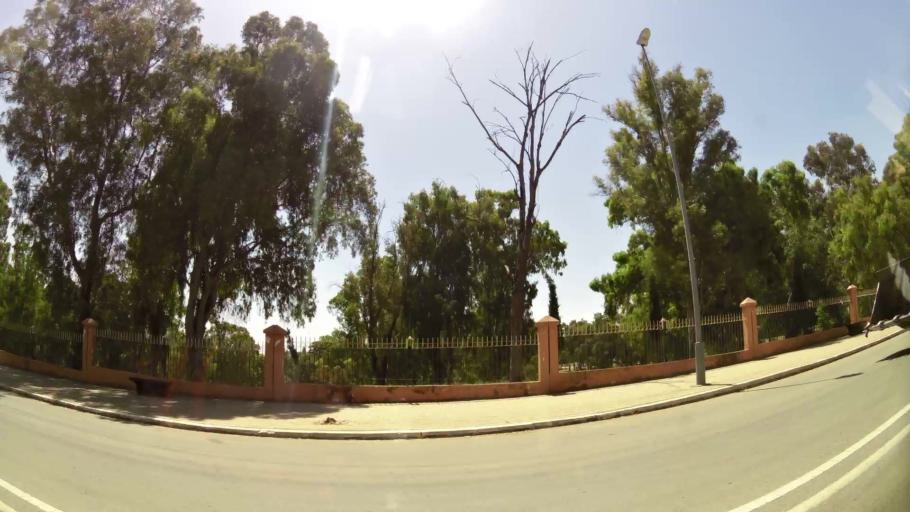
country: MA
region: Rabat-Sale-Zemmour-Zaer
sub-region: Khemisset
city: Khemisset
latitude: 33.8264
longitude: -6.0612
